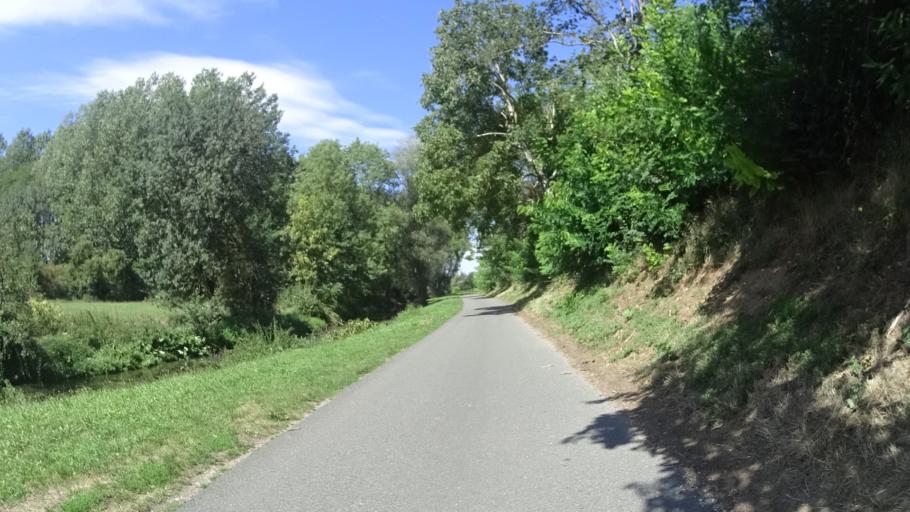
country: FR
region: Centre
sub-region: Departement du Loiret
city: Bonny-sur-Loire
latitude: 47.5657
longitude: 2.8304
